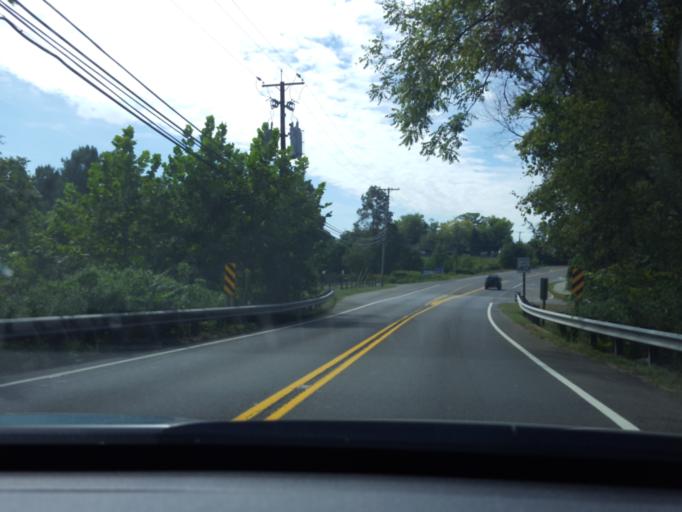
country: US
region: Maryland
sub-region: Prince George's County
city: Mellwood
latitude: 38.8016
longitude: -76.8253
